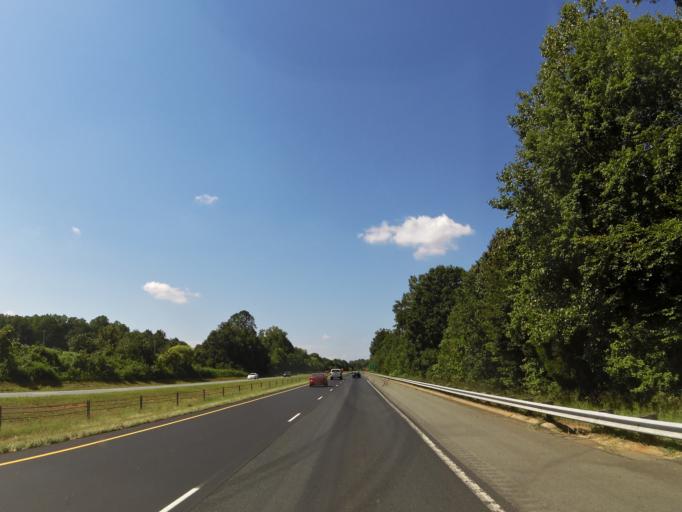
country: US
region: North Carolina
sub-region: Lincoln County
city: Lincolnton
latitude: 35.4491
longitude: -81.2153
